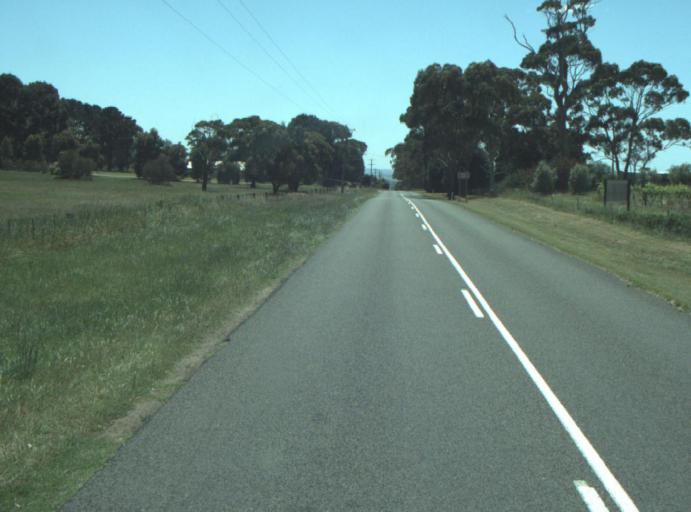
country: AU
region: Victoria
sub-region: Greater Geelong
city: Lara
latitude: -37.8835
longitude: 144.2598
